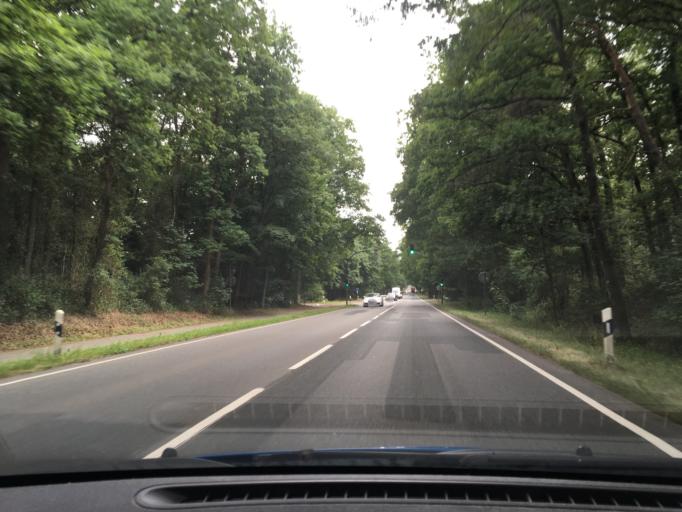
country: DE
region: Lower Saxony
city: Kakenstorf
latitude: 53.3065
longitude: 9.7566
